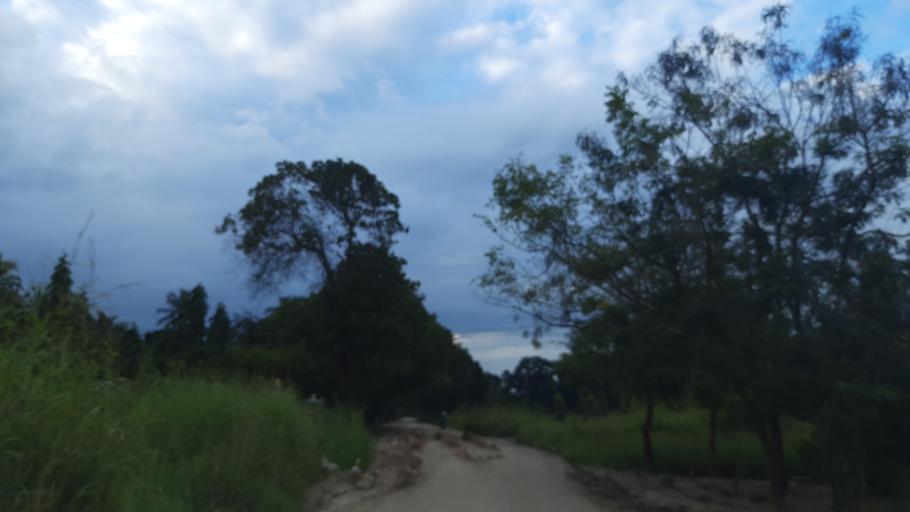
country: TZ
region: Pwani
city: Bagamoyo
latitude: -6.5170
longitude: 38.9288
